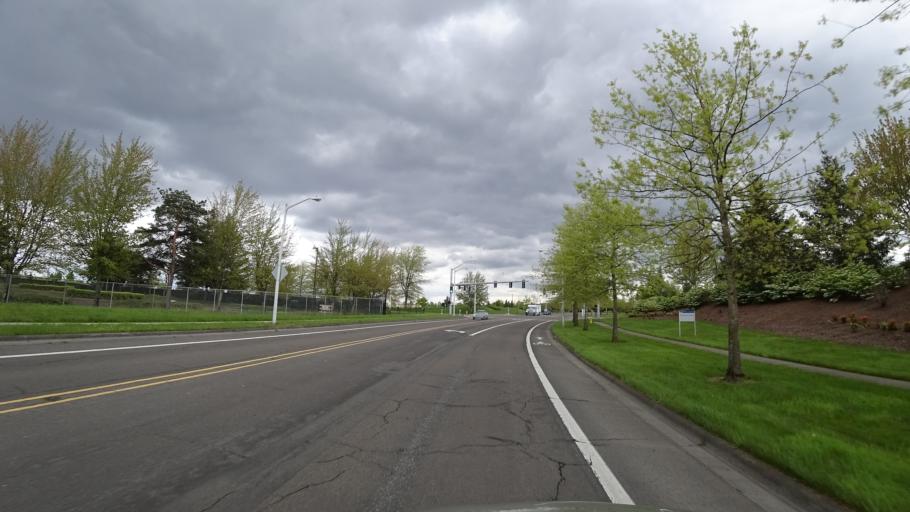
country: US
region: Oregon
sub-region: Washington County
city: Rockcreek
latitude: 45.5420
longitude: -122.9077
